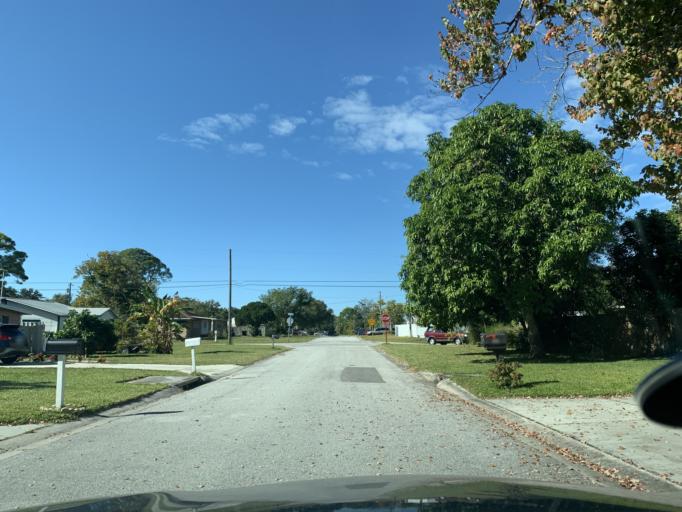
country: US
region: Florida
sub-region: Pinellas County
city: Kenneth City
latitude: 27.8174
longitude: -82.7491
